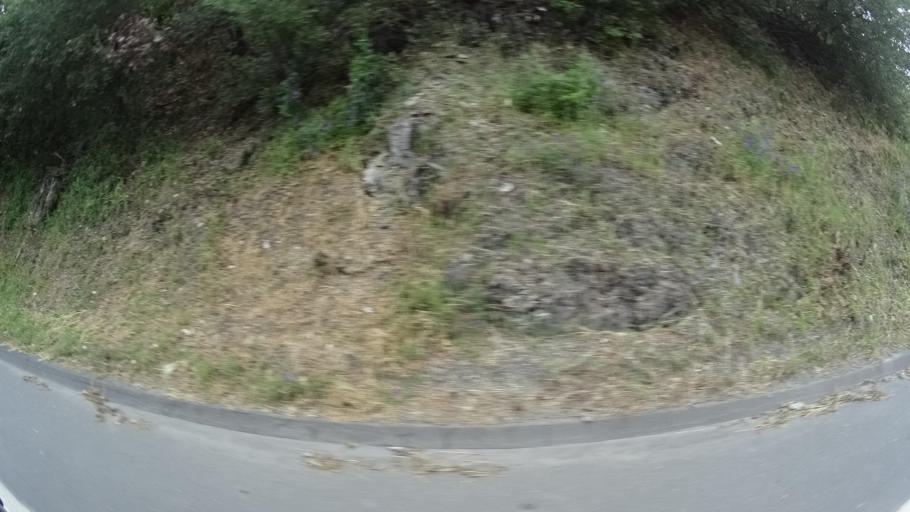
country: US
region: California
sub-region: Humboldt County
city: Willow Creek
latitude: 40.9415
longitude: -123.6320
